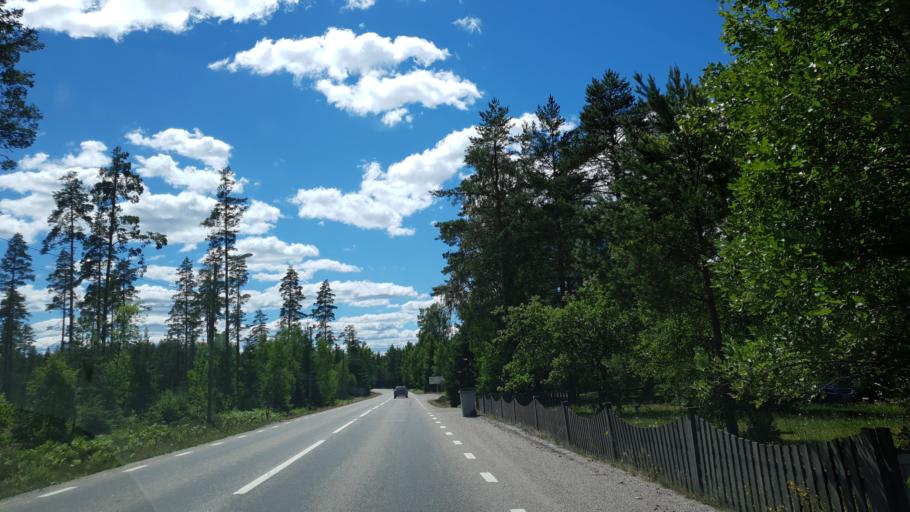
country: SE
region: Kronoberg
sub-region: Lessebo Kommun
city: Lessebo
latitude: 56.8205
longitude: 15.3803
